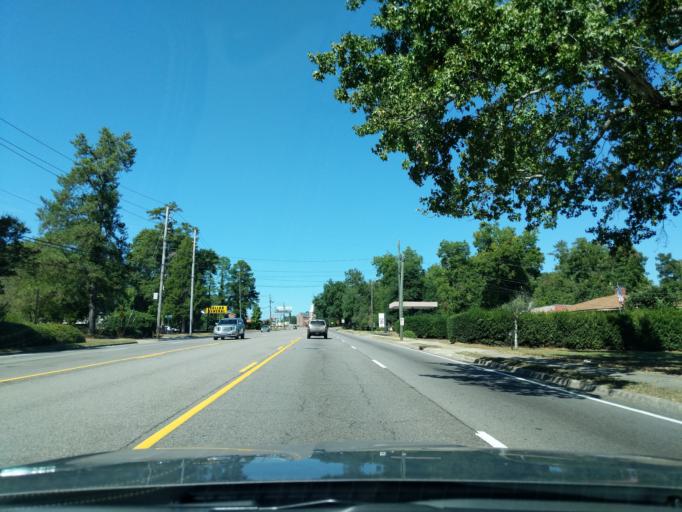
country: US
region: Georgia
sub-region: Richmond County
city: Augusta
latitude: 33.4958
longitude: -82.0107
